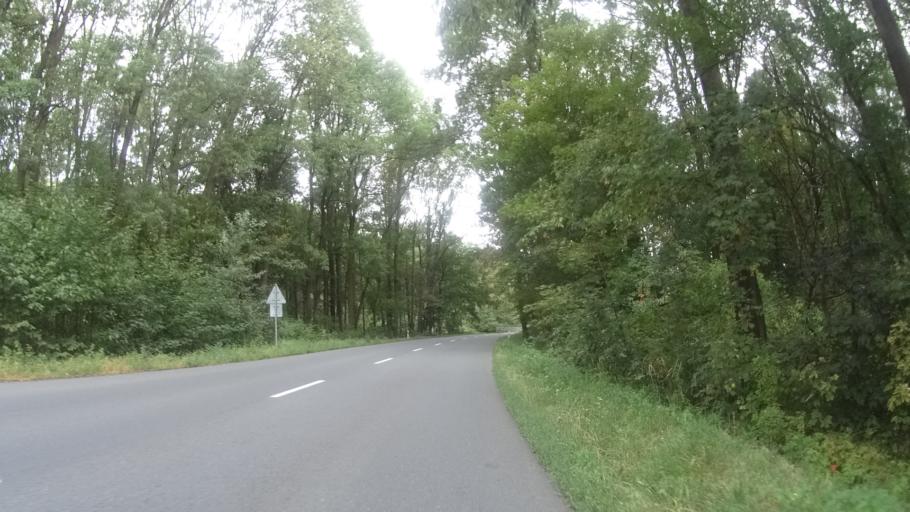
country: CZ
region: Zlin
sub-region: Okres Kromeriz
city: Kromeriz
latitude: 49.3276
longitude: 17.3871
